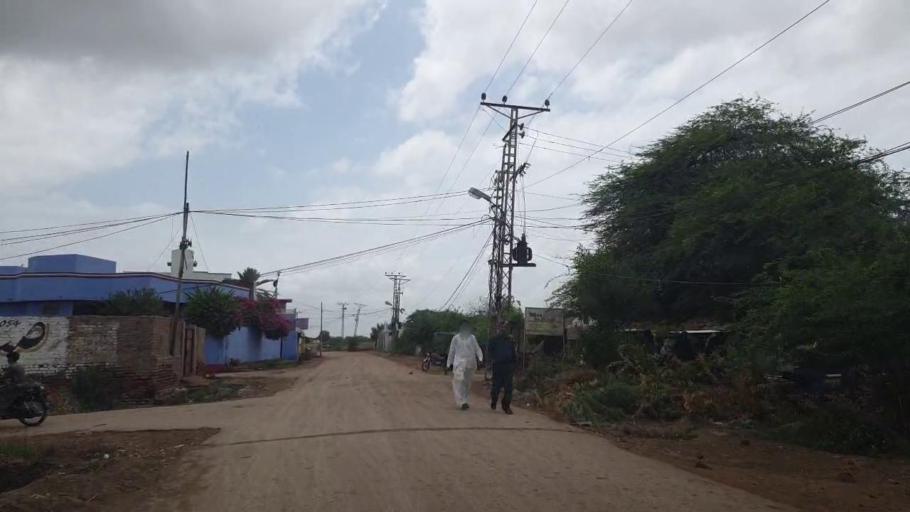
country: PK
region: Sindh
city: Badin
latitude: 24.6555
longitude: 68.8479
